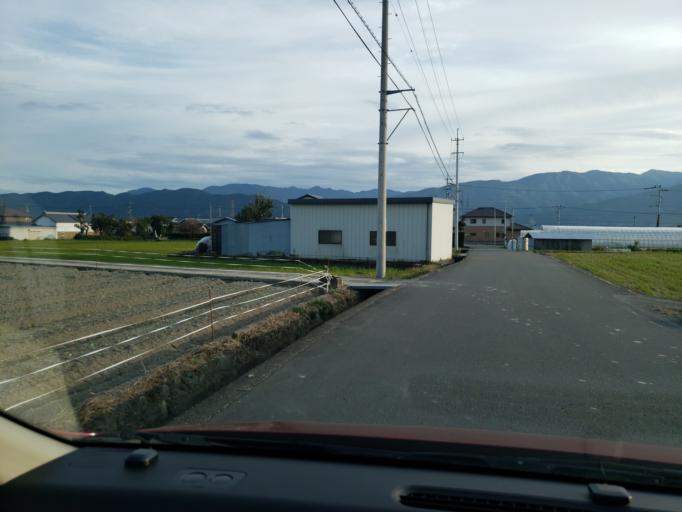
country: JP
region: Tokushima
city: Wakimachi
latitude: 34.0840
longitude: 134.2270
